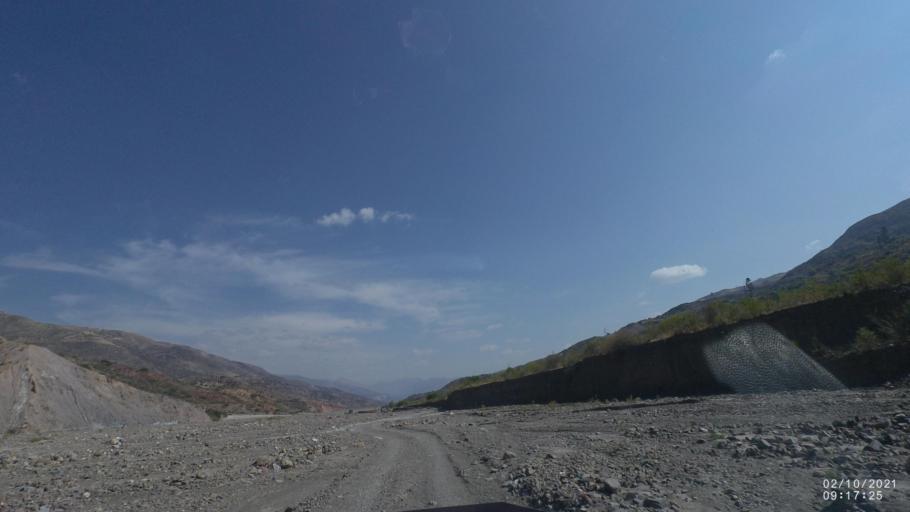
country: BO
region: Cochabamba
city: Irpa Irpa
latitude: -17.8814
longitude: -66.3048
